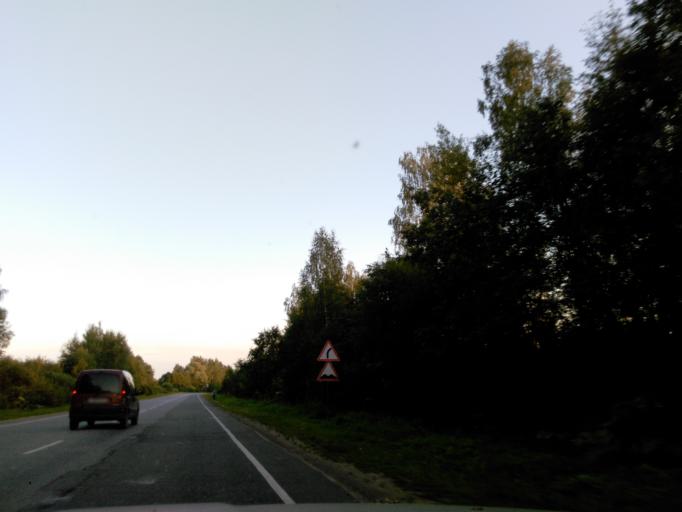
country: RU
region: Tverskaya
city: Konakovo
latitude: 56.6455
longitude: 36.7089
